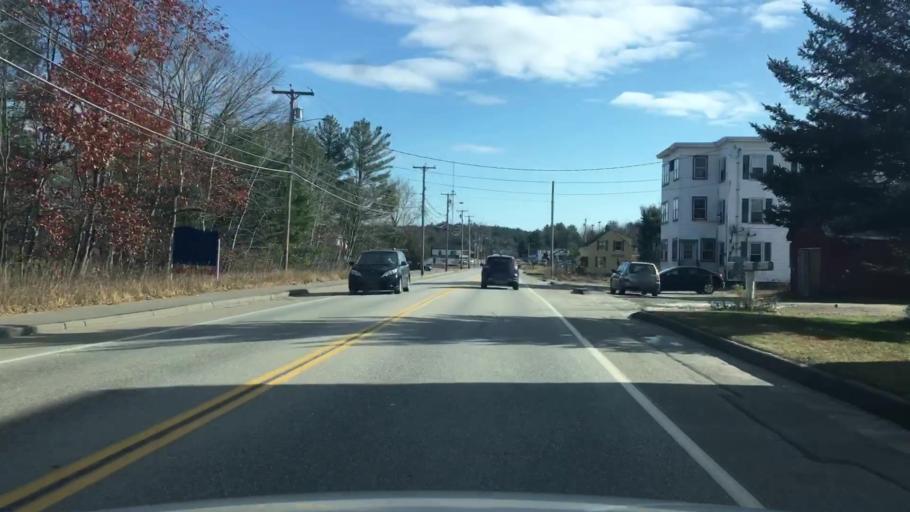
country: US
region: Maine
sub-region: Kennebec County
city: Augusta
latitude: 44.3053
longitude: -69.7466
